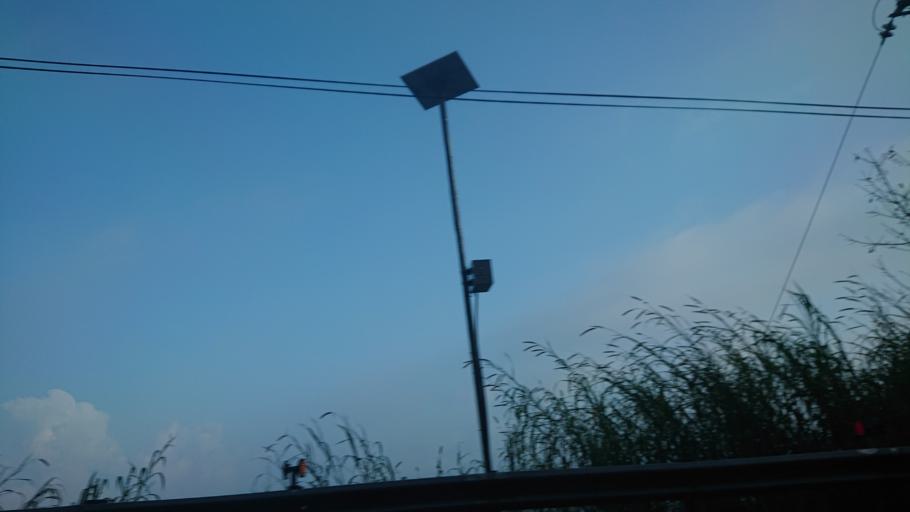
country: TW
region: Taiwan
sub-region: Chiayi
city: Jiayi Shi
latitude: 23.4596
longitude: 120.7234
